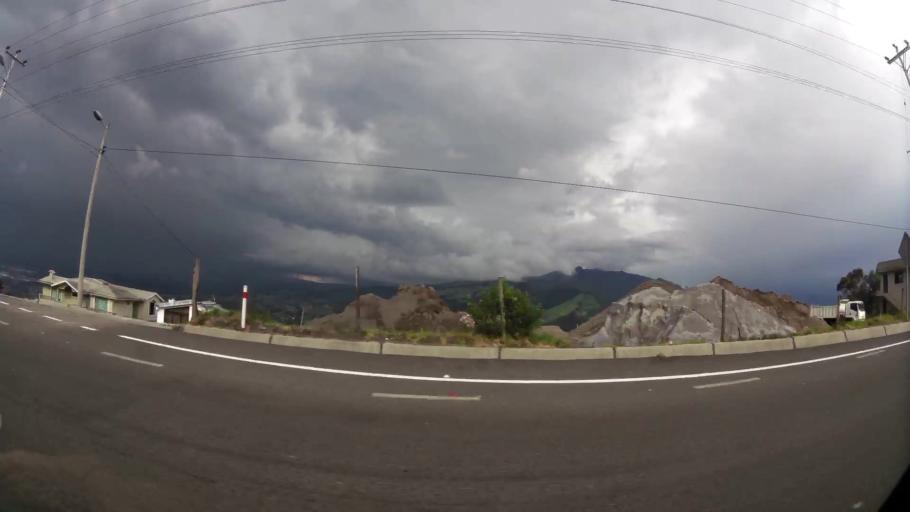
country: EC
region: Pichincha
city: Sangolqui
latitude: -0.3866
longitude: -78.5346
